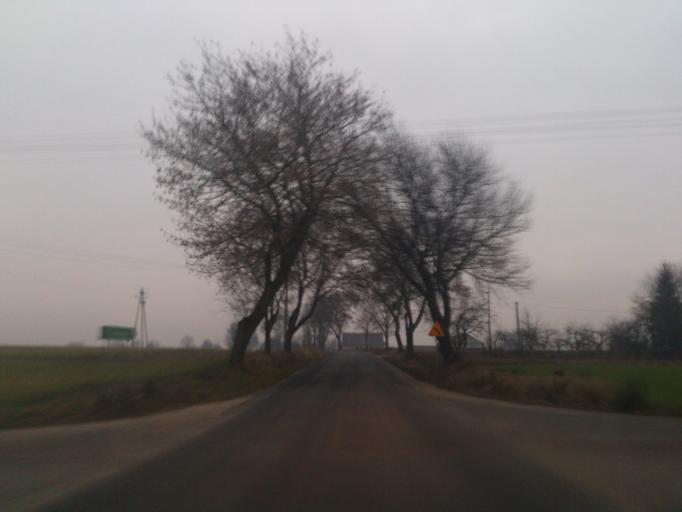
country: PL
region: Kujawsko-Pomorskie
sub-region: Powiat rypinski
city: Wapielsk
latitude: 53.2007
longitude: 19.2327
